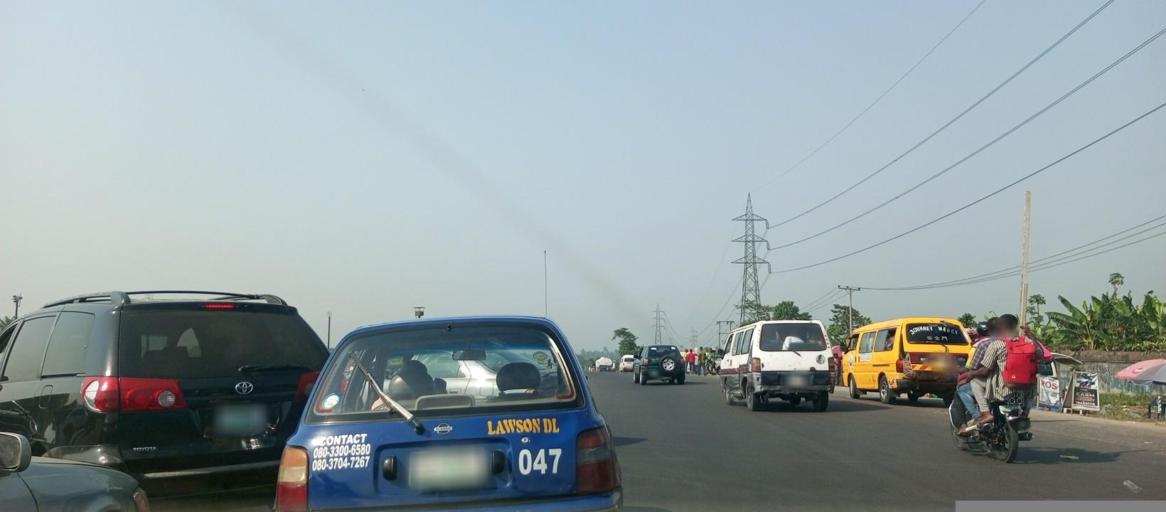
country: NG
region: Rivers
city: Emuoha
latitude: 4.8986
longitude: 6.9029
